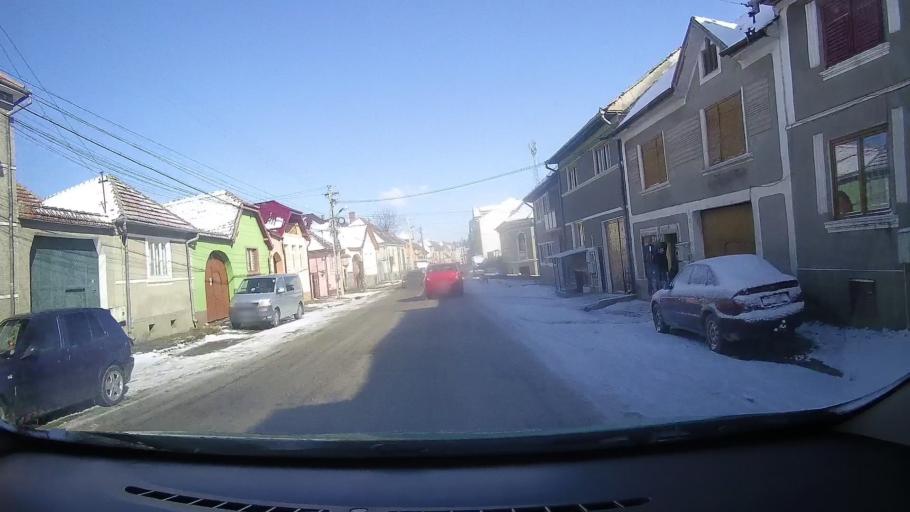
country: RO
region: Sibiu
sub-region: Comuna Avrig
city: Avrig
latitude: 45.7254
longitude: 24.3743
